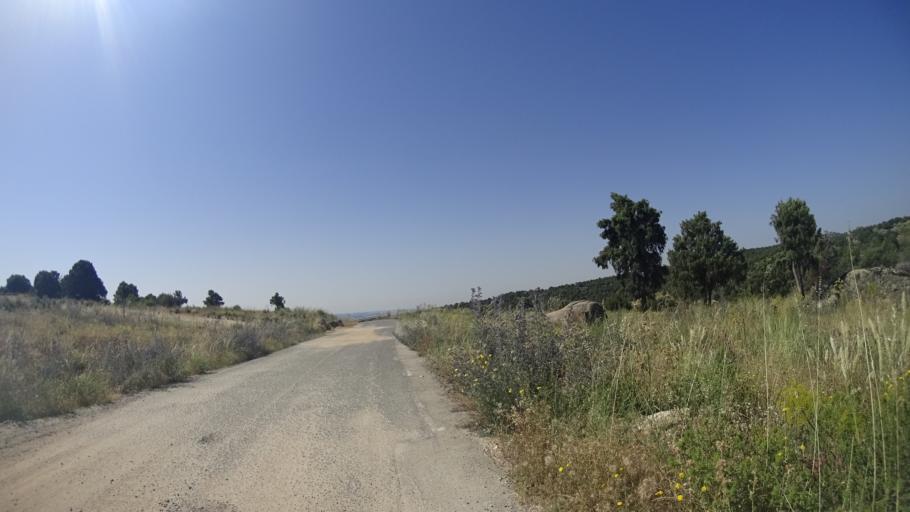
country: ES
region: Madrid
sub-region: Provincia de Madrid
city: Hoyo de Manzanares
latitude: 40.6006
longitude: -3.9004
